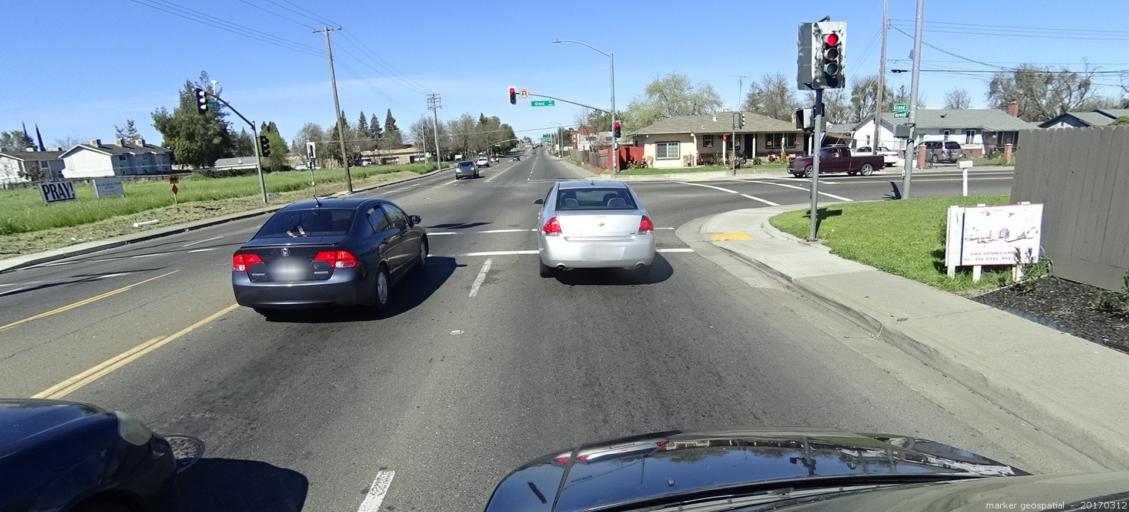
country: US
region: California
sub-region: Sacramento County
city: Rio Linda
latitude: 38.6366
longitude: -121.4569
